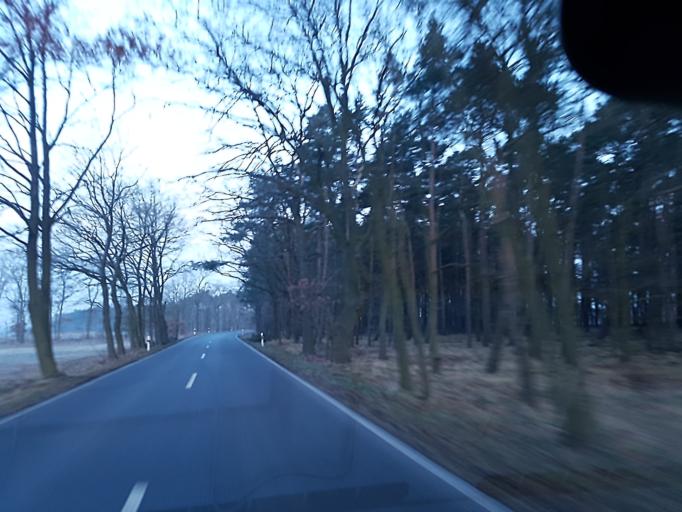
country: DE
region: Saxony-Anhalt
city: Holzdorf
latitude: 51.7561
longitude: 13.1204
